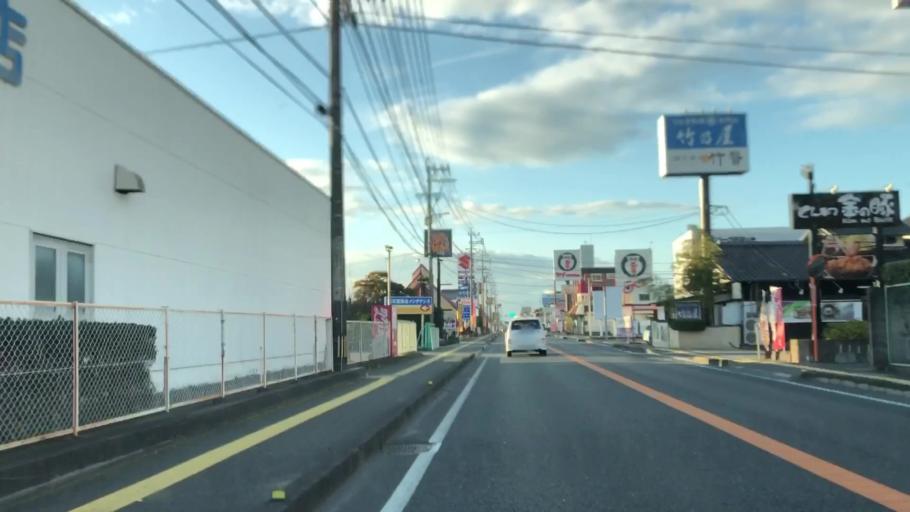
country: JP
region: Oita
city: Bungo-Takada-shi
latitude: 33.5309
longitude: 131.3353
